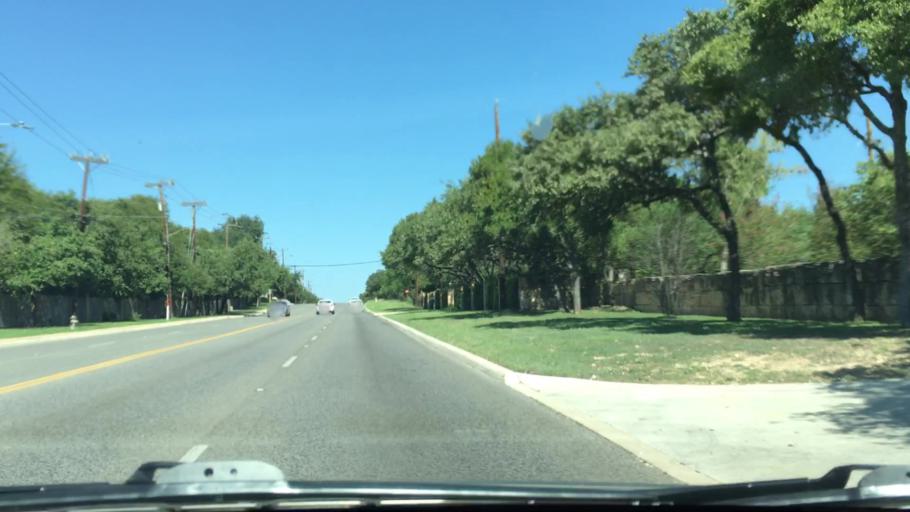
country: US
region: Texas
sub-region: Bexar County
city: Hollywood Park
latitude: 29.5728
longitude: -98.4925
